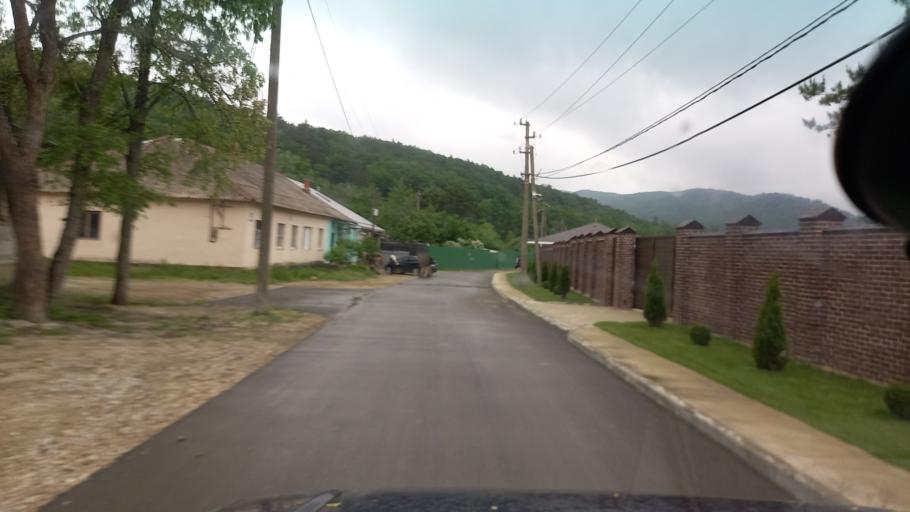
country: RU
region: Krasnodarskiy
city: Azovskaya
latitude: 44.6403
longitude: 38.6158
